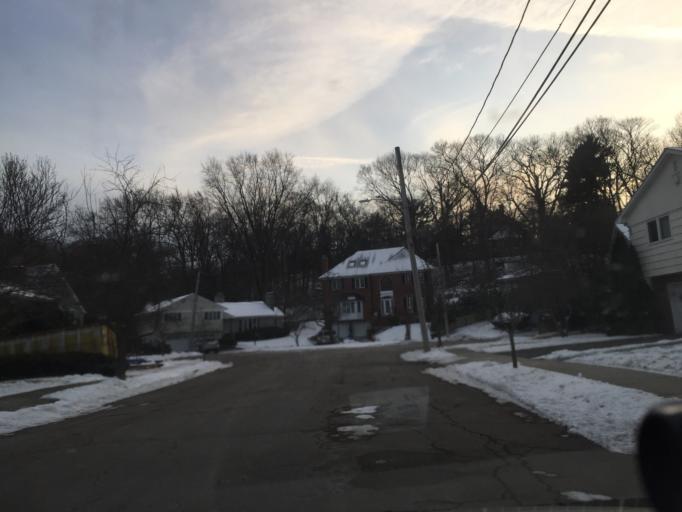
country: US
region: Massachusetts
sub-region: Norfolk County
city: Brookline
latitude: 42.3313
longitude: -71.1539
